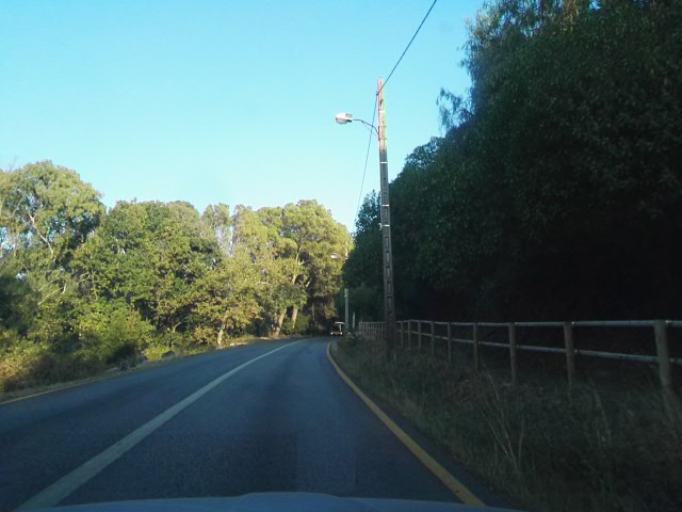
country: PT
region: Lisbon
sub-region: Odivelas
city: Pontinha
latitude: 38.7247
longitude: -9.1903
